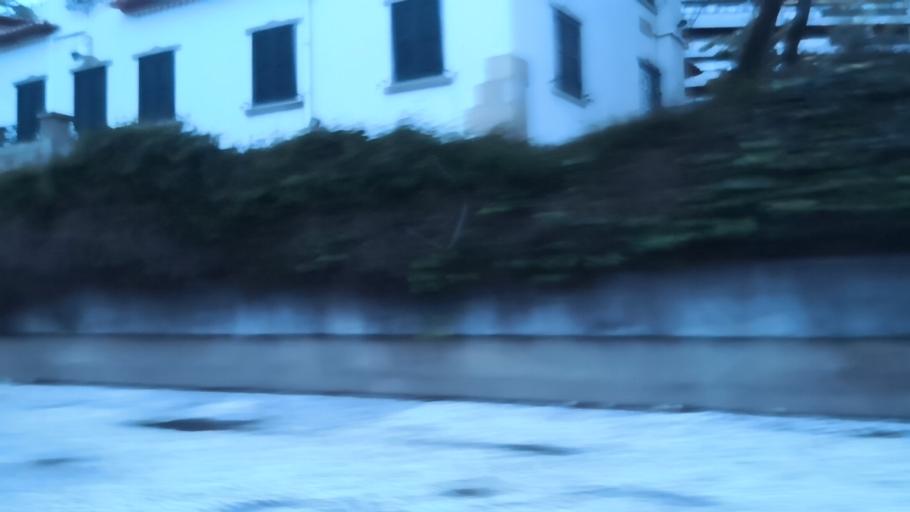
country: PT
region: Porto
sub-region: Vila Nova de Gaia
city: Oliveira do Douro
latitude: 41.1435
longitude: -8.5860
